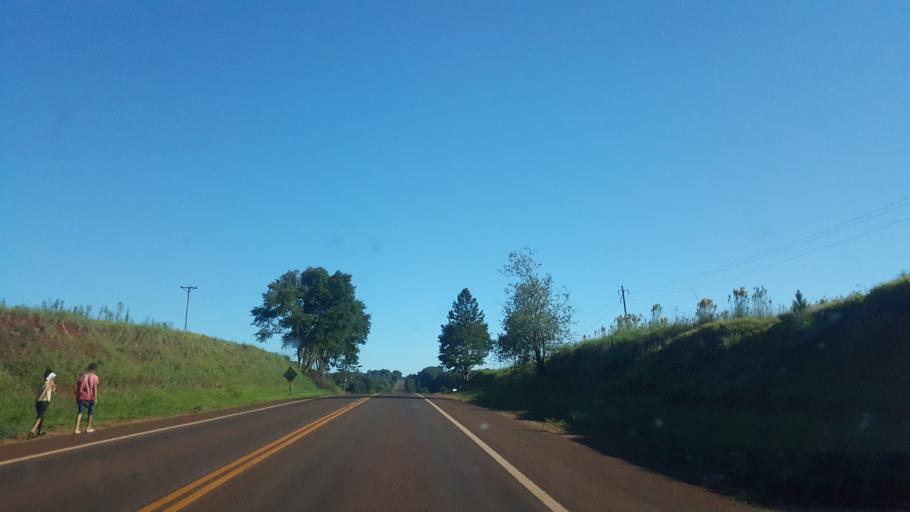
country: AR
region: Misiones
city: Puerto Esperanza
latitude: -26.1461
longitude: -54.5826
